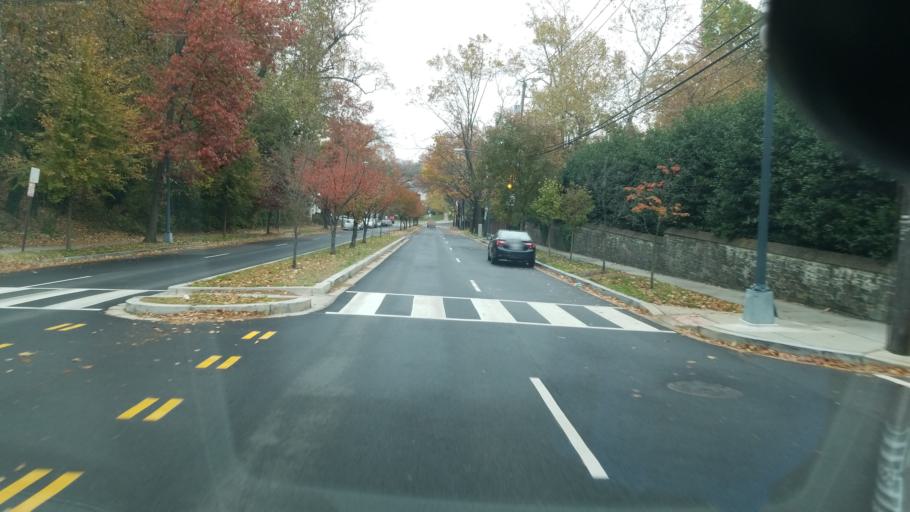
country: US
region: Washington, D.C.
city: Washington, D.C.
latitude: 38.9245
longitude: -77.0594
